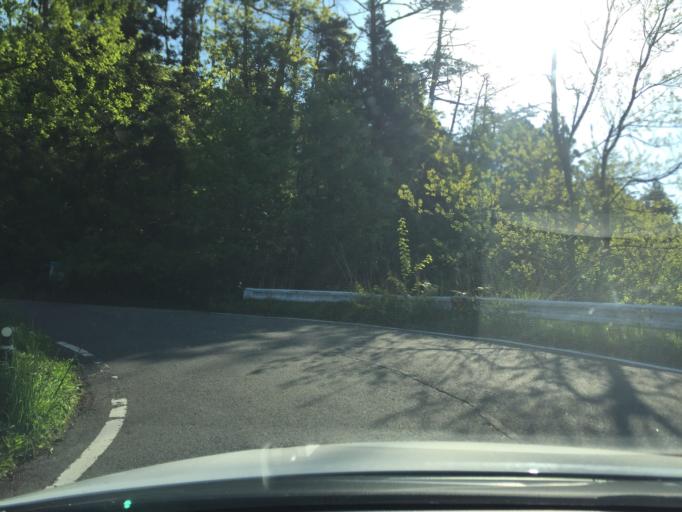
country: JP
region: Fukushima
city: Kitakata
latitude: 37.6686
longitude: 139.8401
